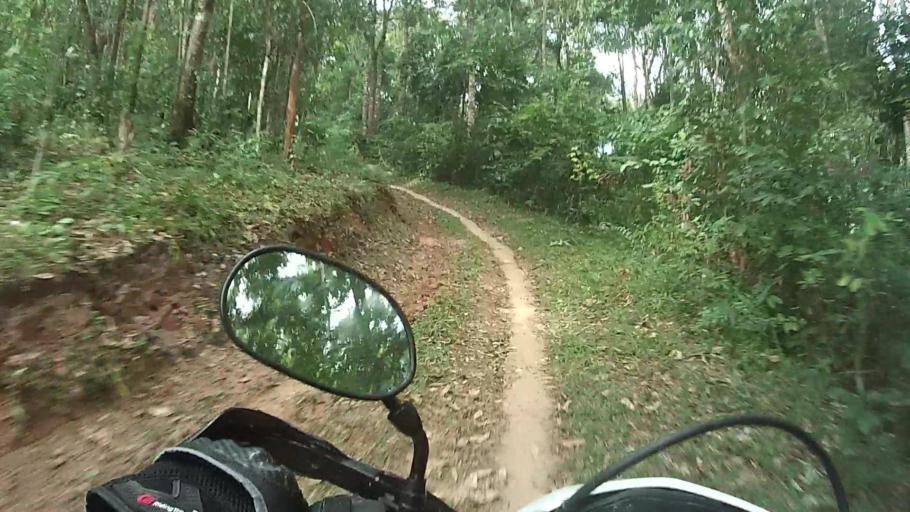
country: TH
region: Lampang
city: Mueang Pan
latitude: 18.8124
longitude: 99.3881
